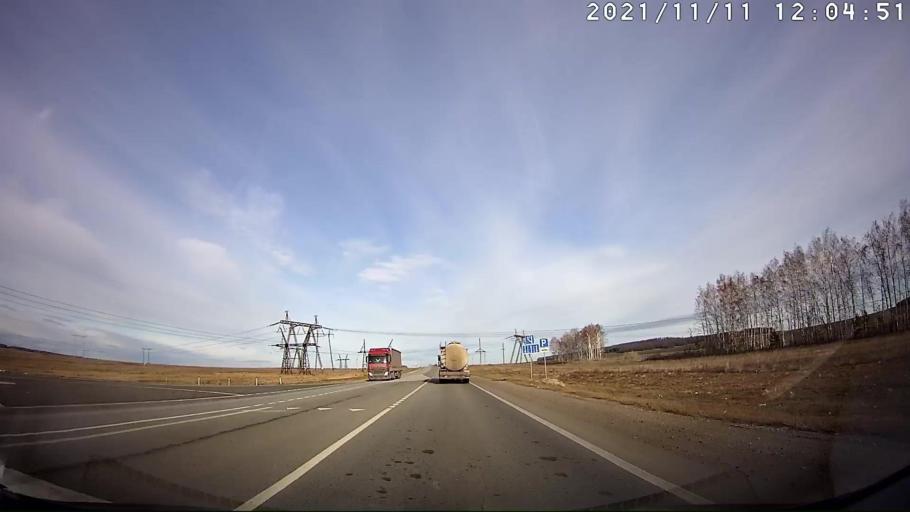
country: RU
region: Ulyanovsk
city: Silikatnyy
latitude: 53.6628
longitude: 48.3504
